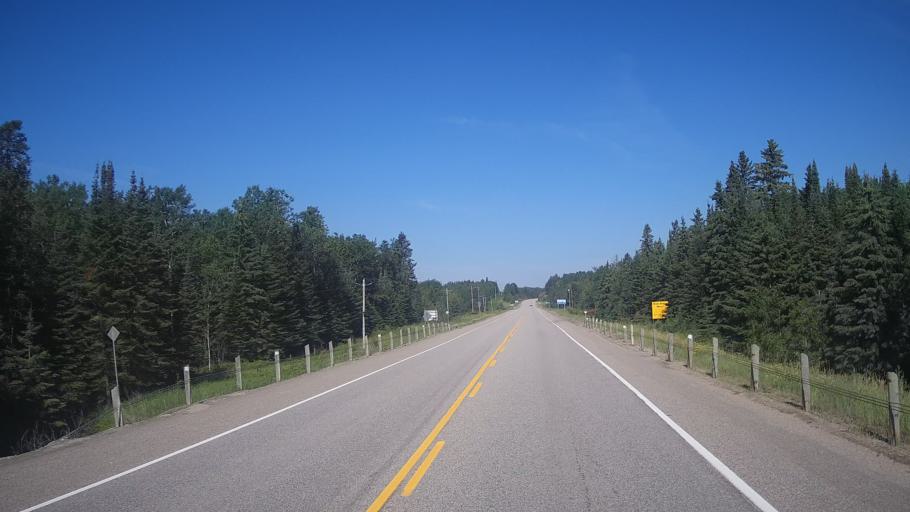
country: CA
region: Ontario
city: Dryden
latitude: 49.7602
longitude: -92.6608
